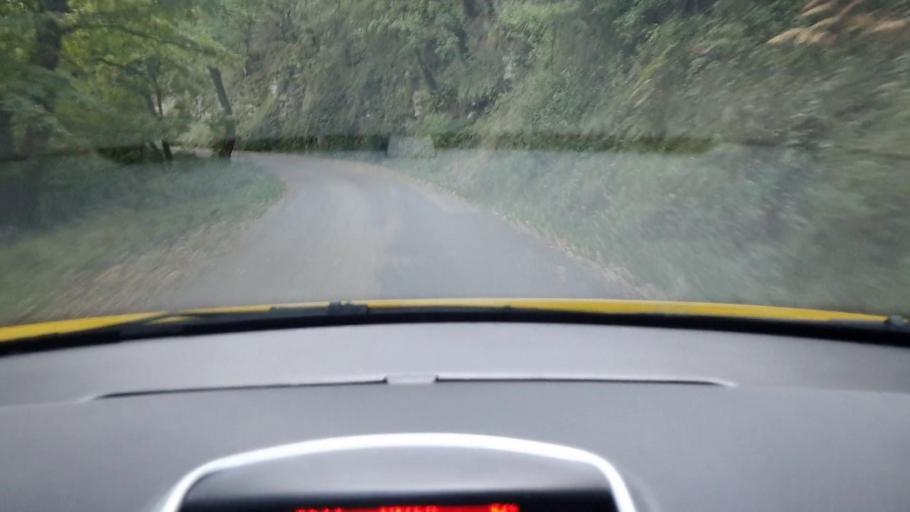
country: FR
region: Languedoc-Roussillon
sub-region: Departement du Gard
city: Sumene
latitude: 43.9741
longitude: 3.7798
